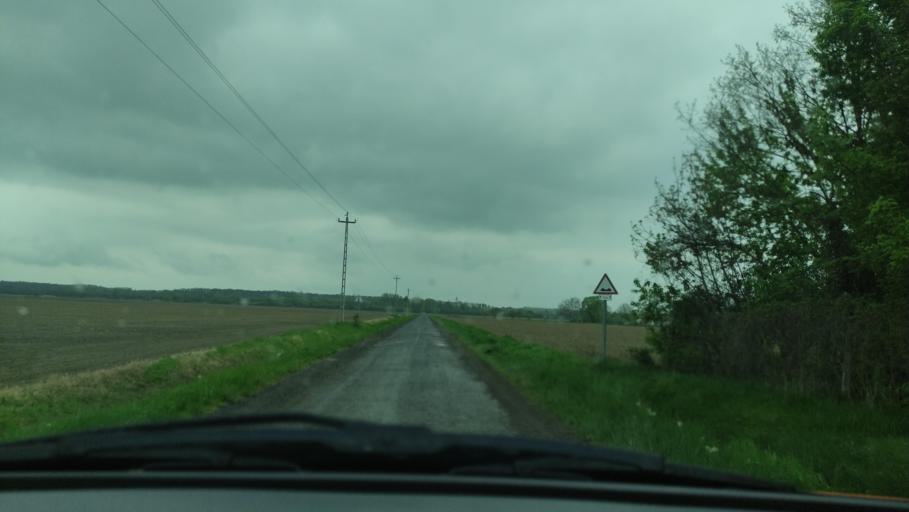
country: HR
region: Osjecko-Baranjska
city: Batina
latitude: 45.9018
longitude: 18.7744
